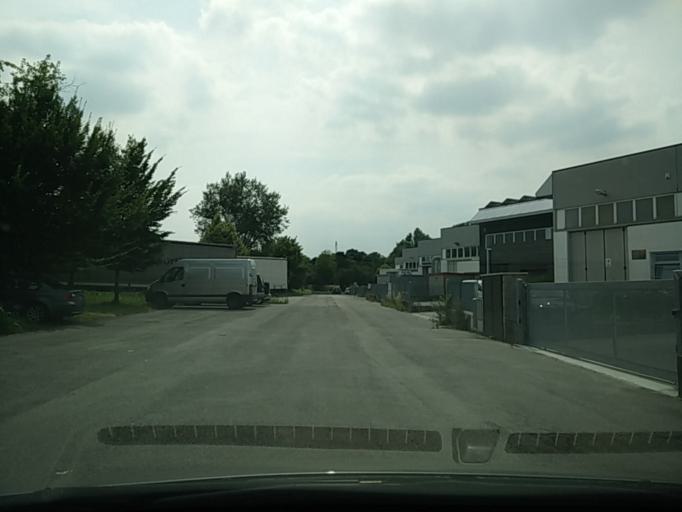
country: IT
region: Veneto
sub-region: Provincia di Treviso
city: Lughignano
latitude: 45.6319
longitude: 12.3122
